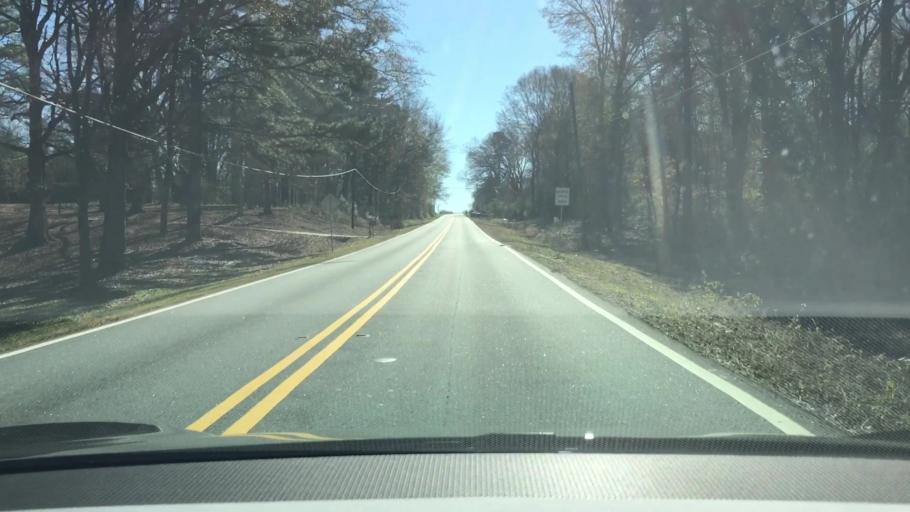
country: US
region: Georgia
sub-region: Walton County
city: Monroe
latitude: 33.8404
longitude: -83.7362
